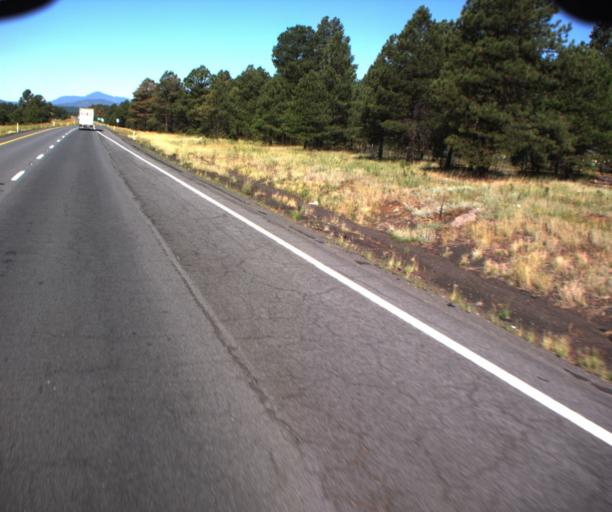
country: US
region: Arizona
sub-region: Coconino County
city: Parks
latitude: 35.2540
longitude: -111.9462
